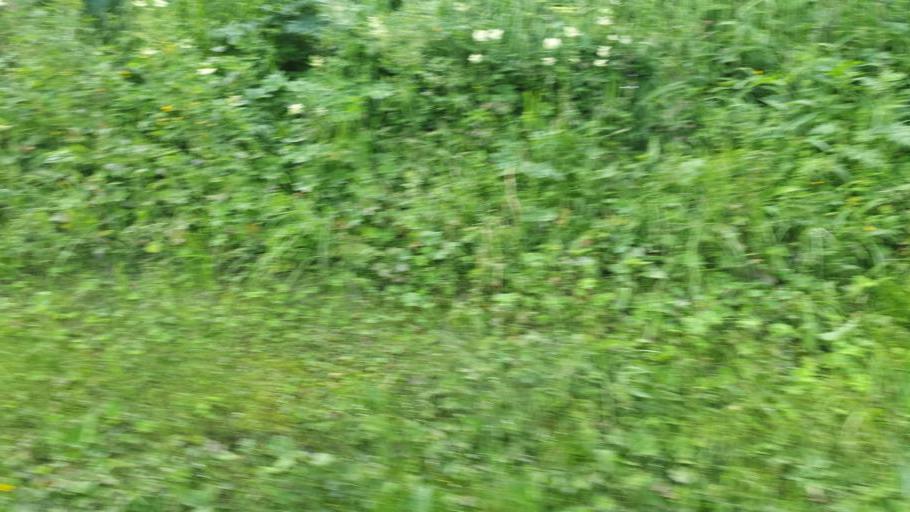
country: NO
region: Sor-Trondelag
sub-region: Midtre Gauldal
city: Storen
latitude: 62.9513
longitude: 10.1868
